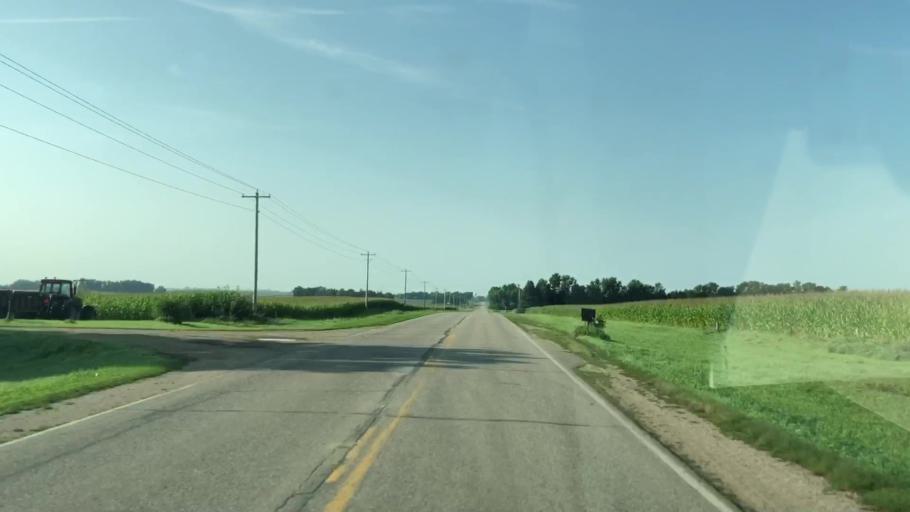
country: US
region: Iowa
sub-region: Lyon County
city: George
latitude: 43.3730
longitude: -95.9982
